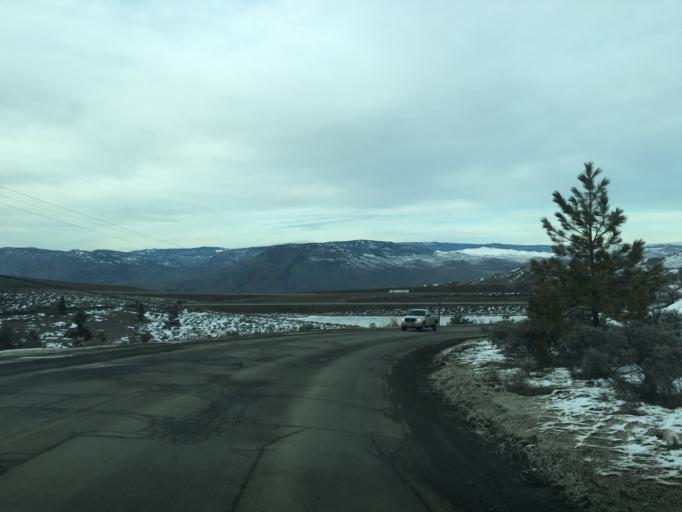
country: CA
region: British Columbia
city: Kamloops
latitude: 50.6607
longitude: -120.4360
